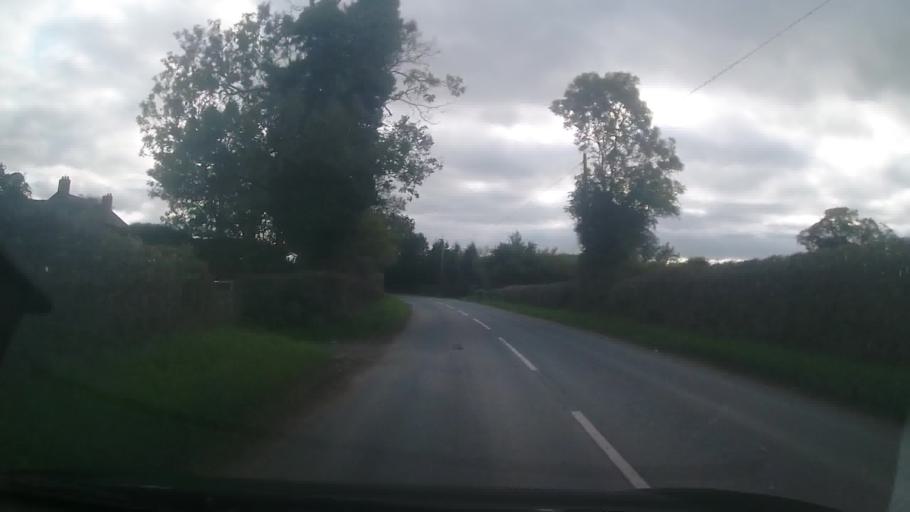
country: GB
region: England
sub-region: Shropshire
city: Bishop's Castle
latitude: 52.4828
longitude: -2.9880
